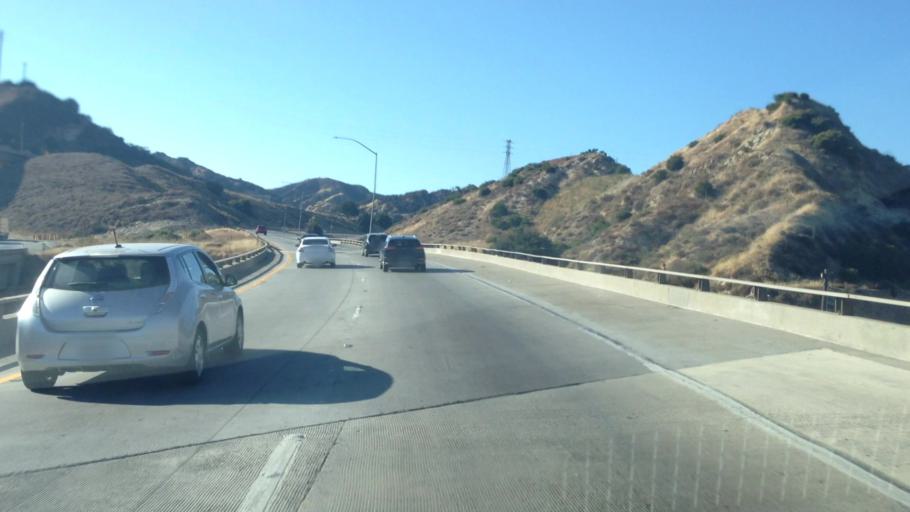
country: US
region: California
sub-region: Los Angeles County
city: Santa Clarita
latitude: 34.3337
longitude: -118.5048
